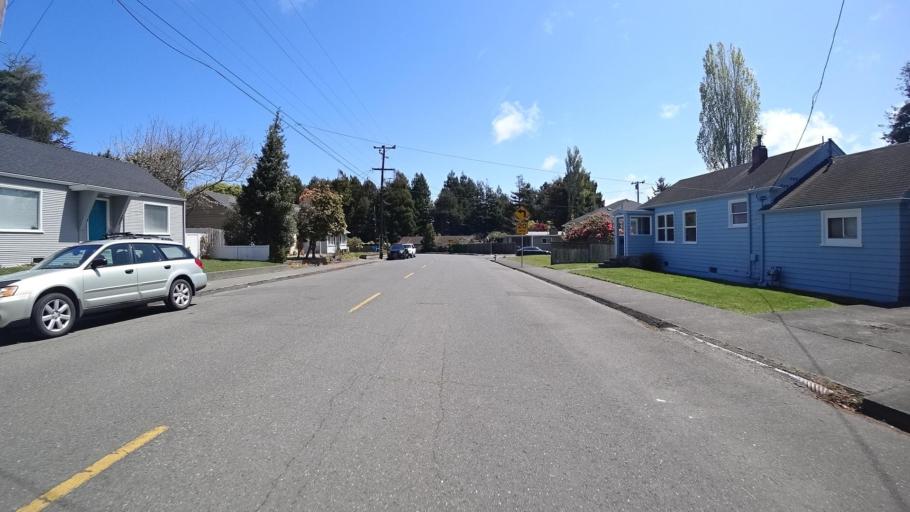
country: US
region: California
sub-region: Humboldt County
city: Eureka
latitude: 40.7904
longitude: -124.1516
